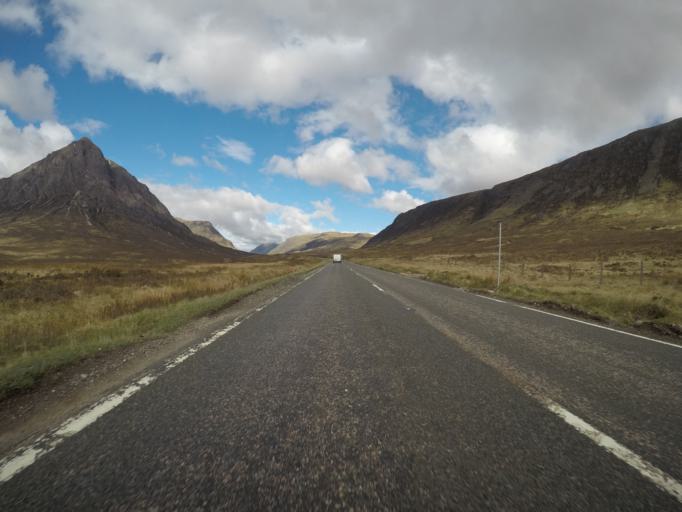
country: GB
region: Scotland
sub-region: Highland
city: Spean Bridge
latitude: 56.6549
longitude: -4.8647
